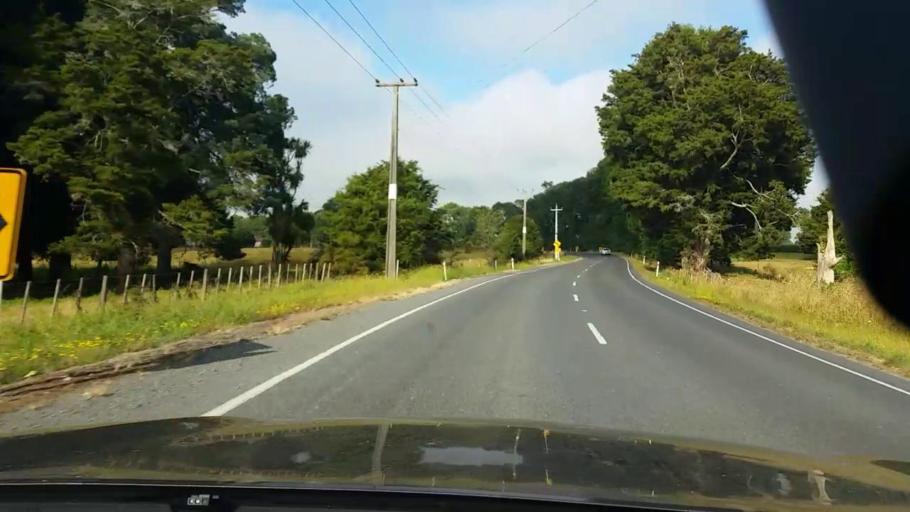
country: NZ
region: Waikato
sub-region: Hamilton City
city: Hamilton
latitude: -37.5973
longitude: 175.3571
